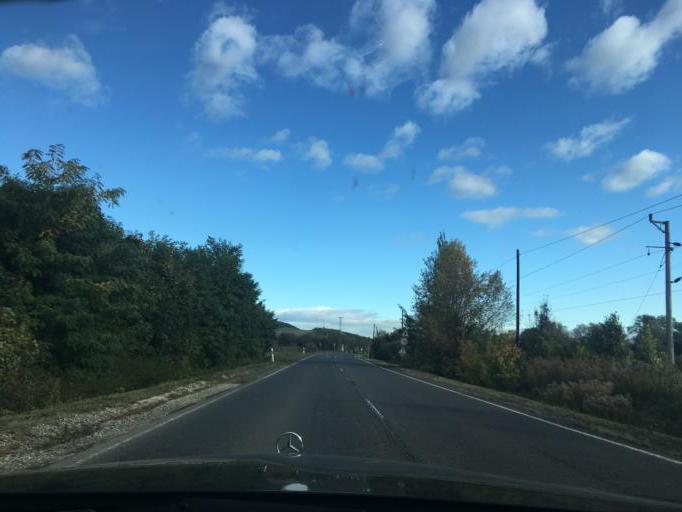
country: HU
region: Borsod-Abauj-Zemplen
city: Gonc
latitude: 48.4761
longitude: 21.2070
